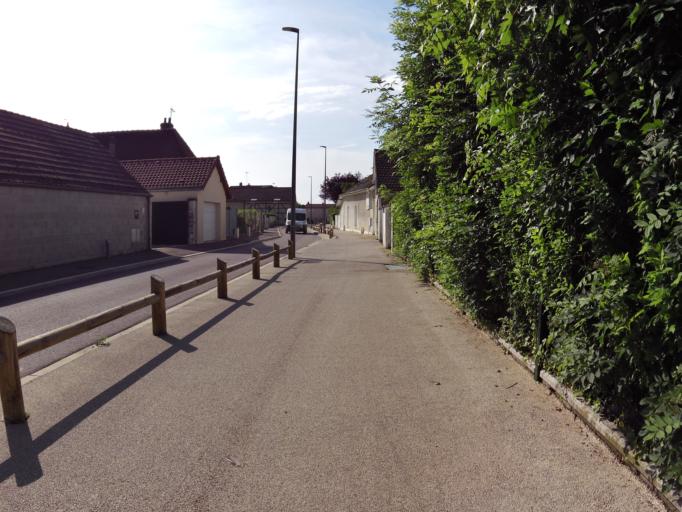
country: FR
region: Champagne-Ardenne
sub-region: Departement de l'Aube
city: Troyes
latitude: 48.2860
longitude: 4.0891
